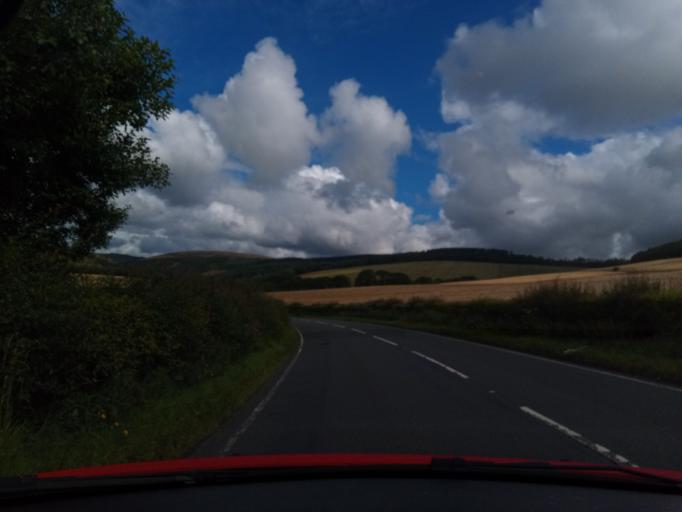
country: GB
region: Scotland
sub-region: The Scottish Borders
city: Lauder
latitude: 55.7263
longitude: -2.7261
